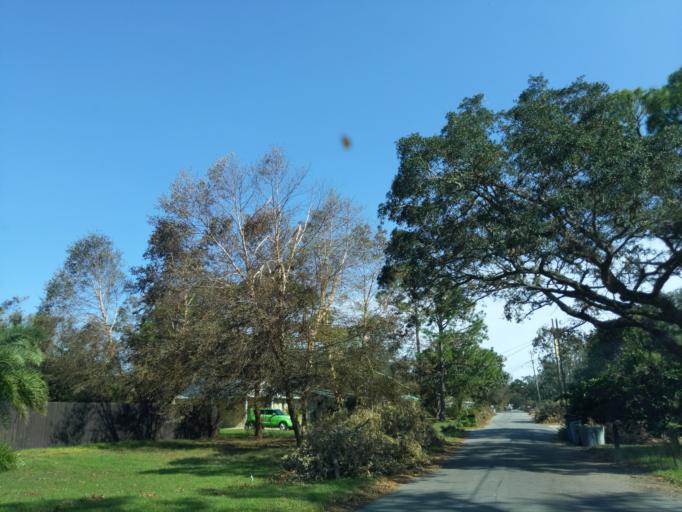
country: US
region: Florida
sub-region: Santa Rosa County
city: Gulf Breeze
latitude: 30.3561
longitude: -87.1916
